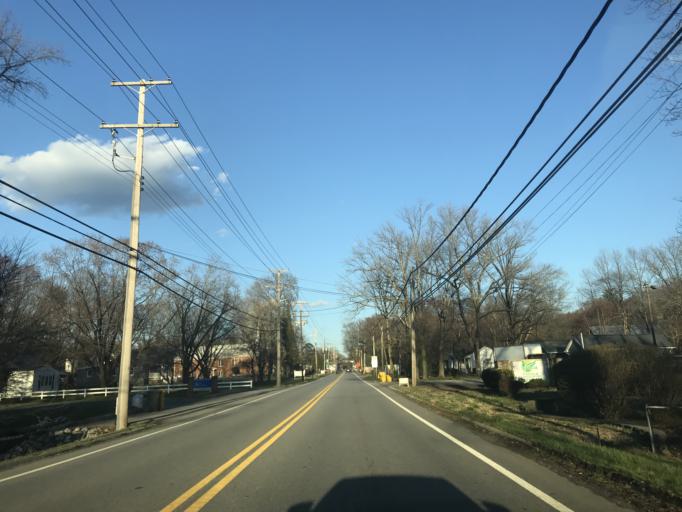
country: US
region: Maryland
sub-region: Anne Arundel County
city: Crofton
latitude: 38.9923
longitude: -76.6759
